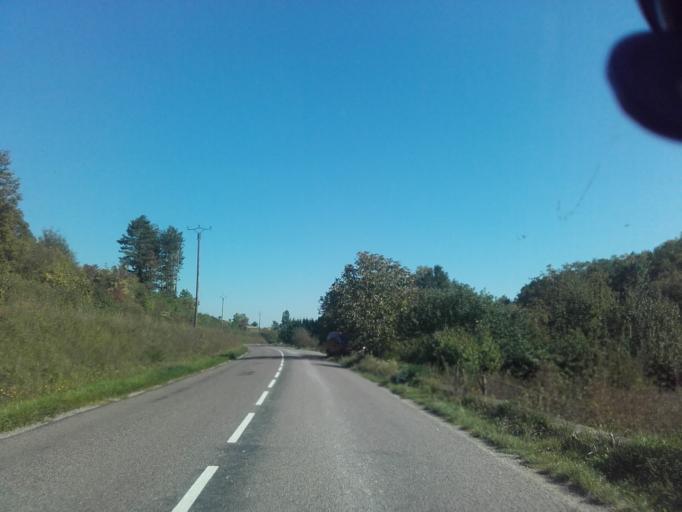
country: FR
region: Bourgogne
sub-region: Departement de la Cote-d'Or
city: Meursault
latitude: 47.0181
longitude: 4.7793
